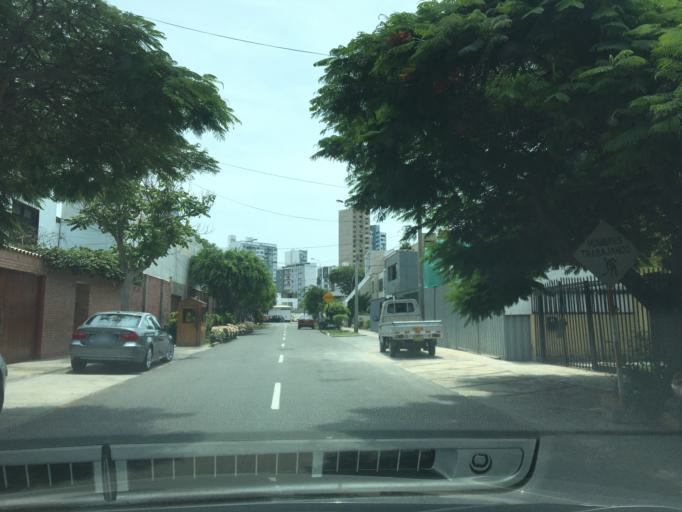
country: PE
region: Lima
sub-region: Lima
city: Surco
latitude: -12.1295
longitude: -77.0255
